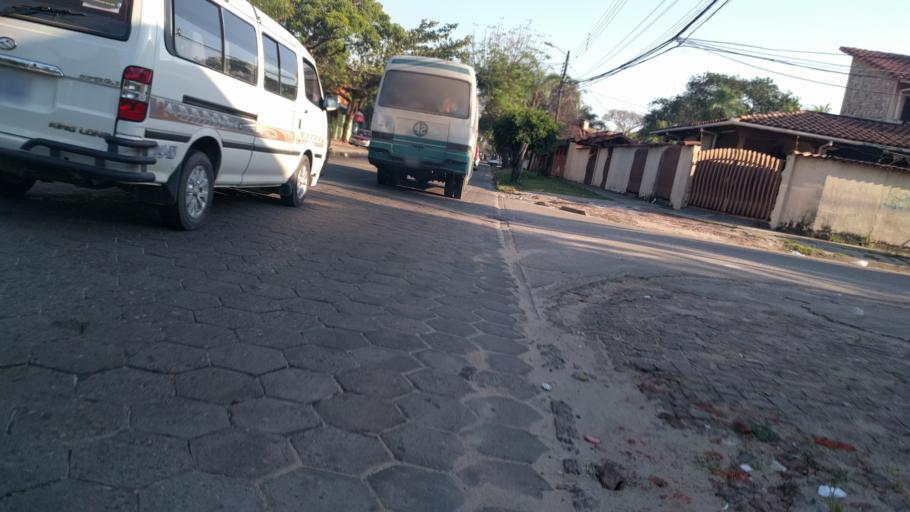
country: BO
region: Santa Cruz
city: Santa Cruz de la Sierra
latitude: -17.8063
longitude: -63.1726
